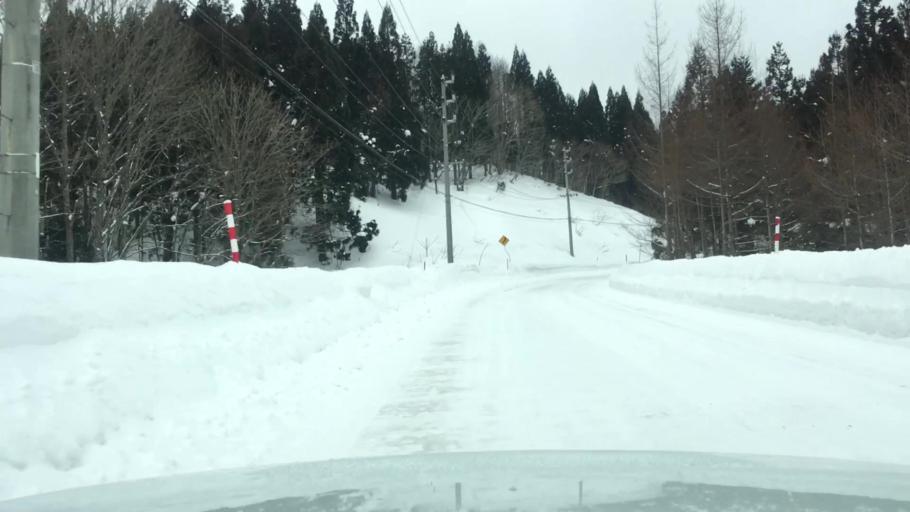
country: JP
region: Akita
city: Hanawa
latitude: 40.0000
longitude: 140.9872
